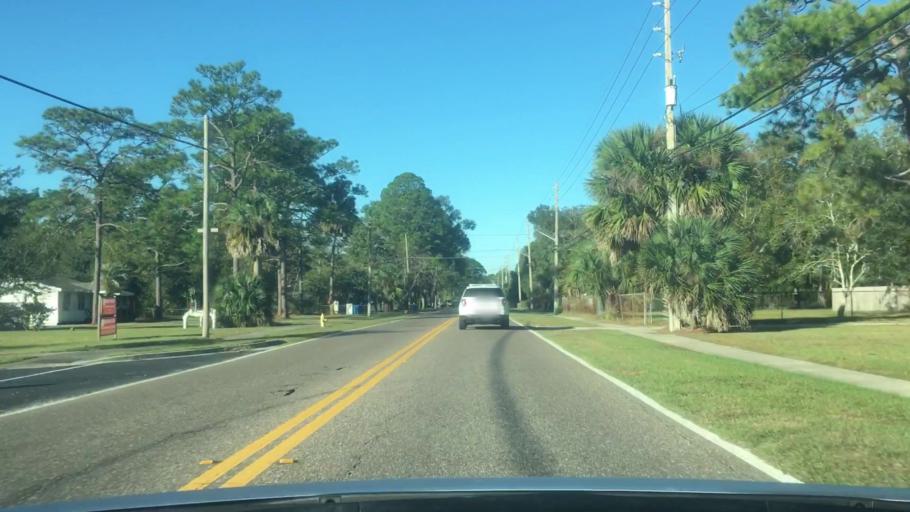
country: US
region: Florida
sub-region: Duval County
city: Jacksonville
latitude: 30.4644
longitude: -81.5867
